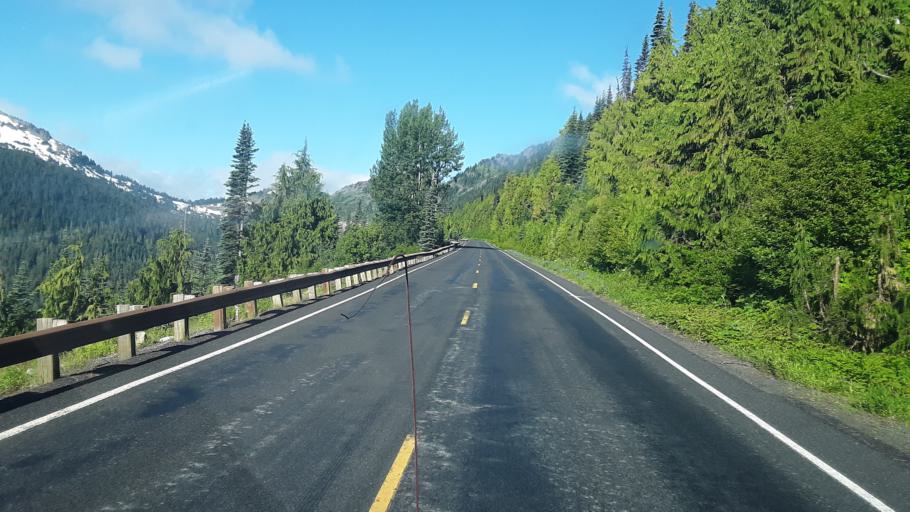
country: US
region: Washington
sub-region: King County
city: Enumclaw
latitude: 46.8938
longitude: -121.4810
